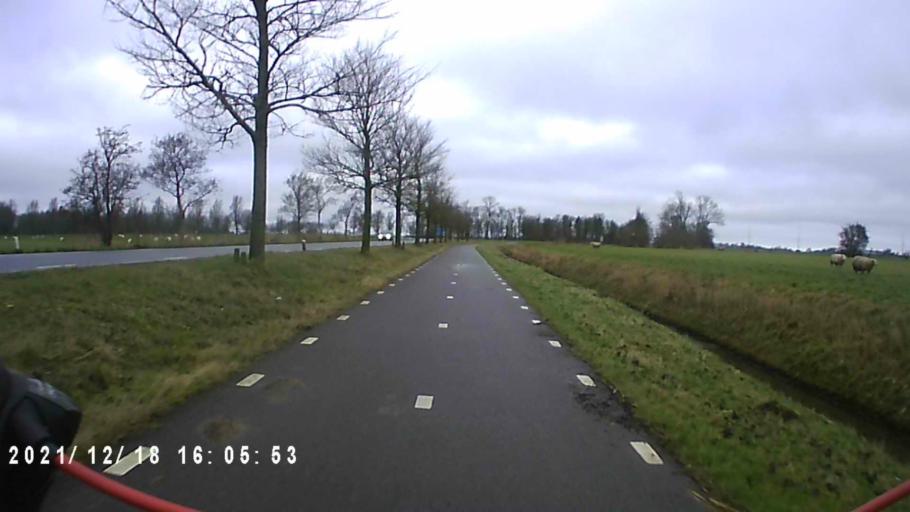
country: NL
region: Friesland
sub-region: Gemeente Dongeradeel
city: Anjum
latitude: 53.3551
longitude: 6.0770
